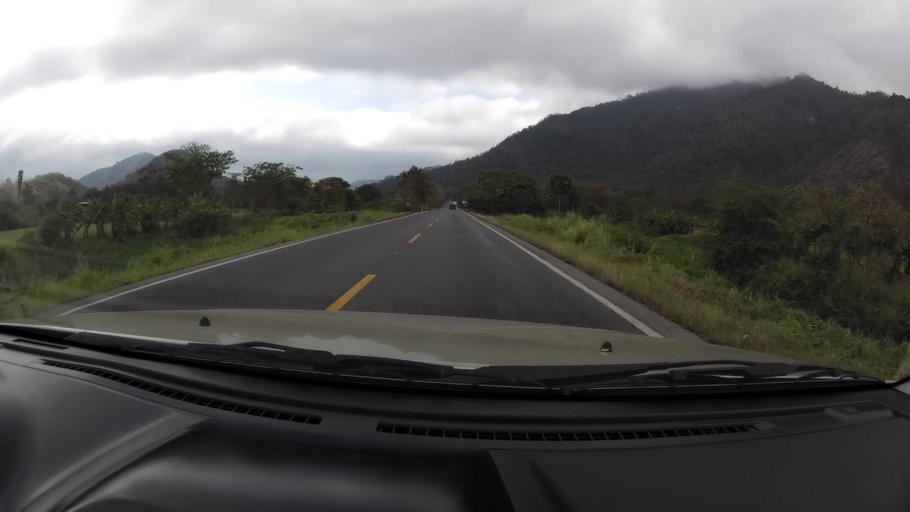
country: EC
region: Guayas
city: Coronel Marcelino Mariduena
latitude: -2.3926
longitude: -79.6304
